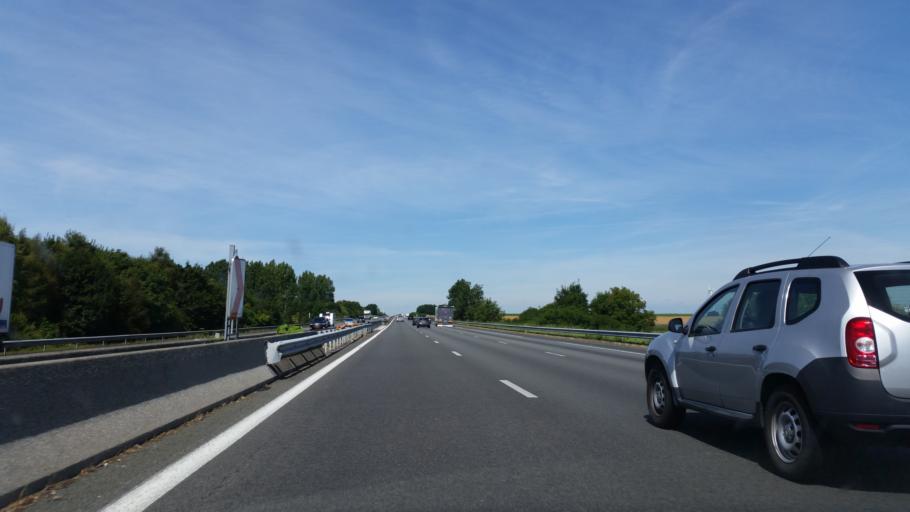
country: FR
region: Nord-Pas-de-Calais
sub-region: Departement du Pas-de-Calais
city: Croisilles
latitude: 50.2046
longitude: 2.8663
